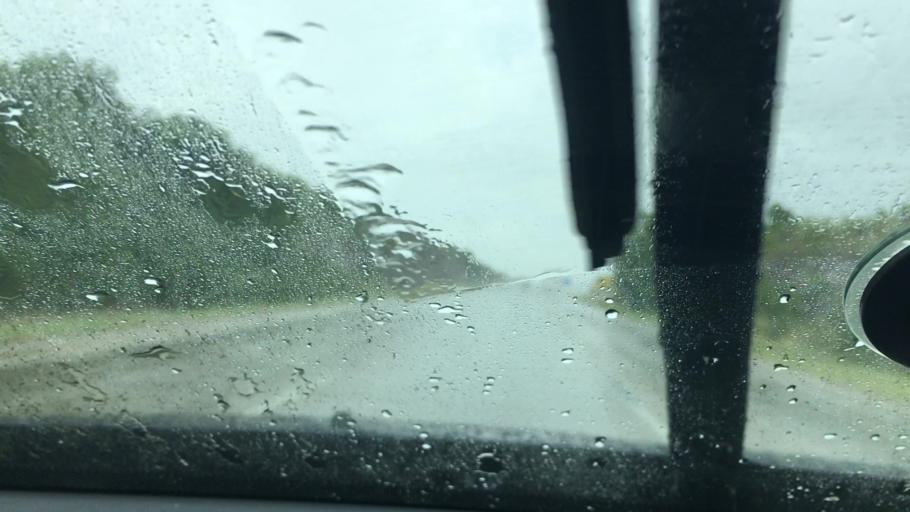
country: US
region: Oklahoma
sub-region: Murray County
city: Davis
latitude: 34.3719
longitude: -97.1454
